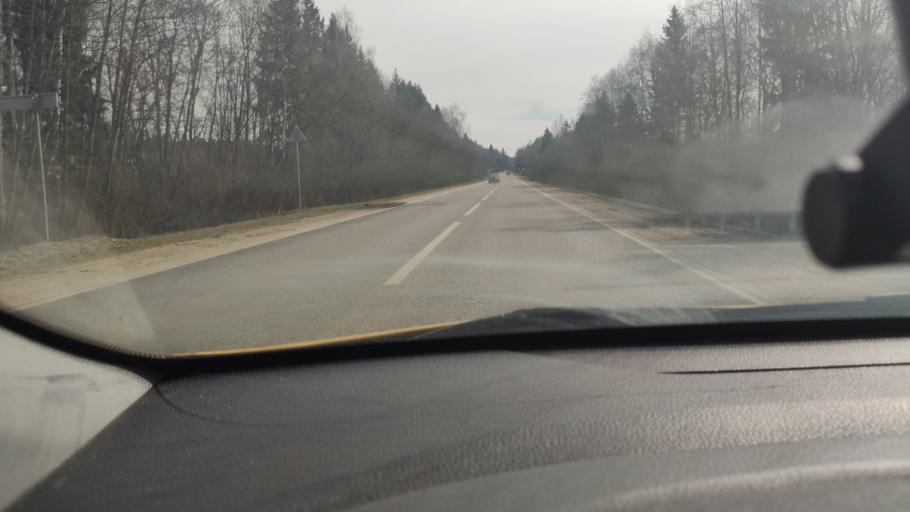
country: RU
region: Moskovskaya
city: Ruza
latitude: 55.7325
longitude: 36.1454
